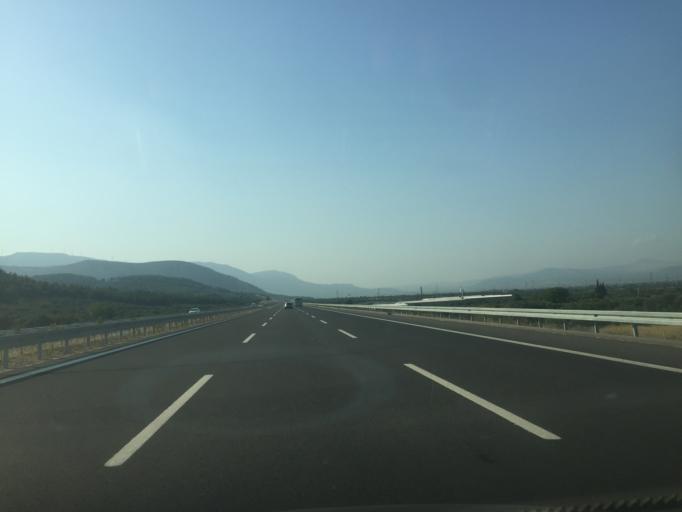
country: TR
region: Manisa
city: Zeytinliova
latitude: 39.0436
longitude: 27.7399
